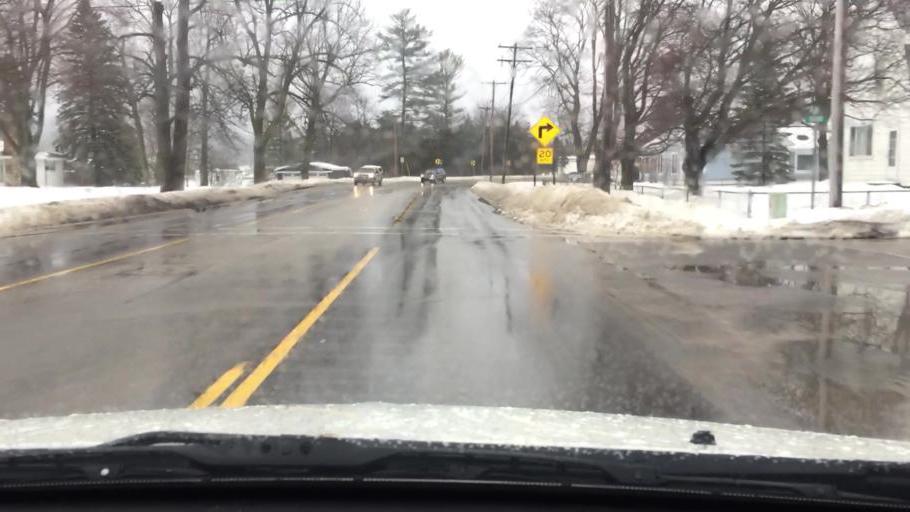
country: US
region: Michigan
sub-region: Charlevoix County
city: East Jordan
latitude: 45.1541
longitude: -85.1361
